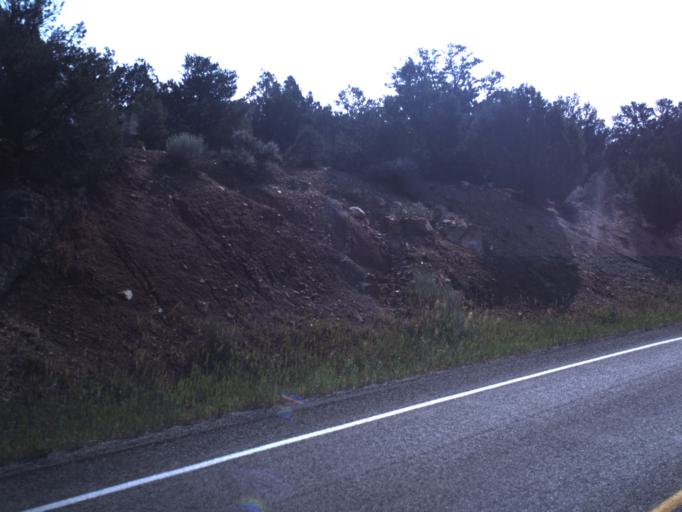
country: US
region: Utah
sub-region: Daggett County
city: Manila
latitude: 40.9530
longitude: -109.4510
